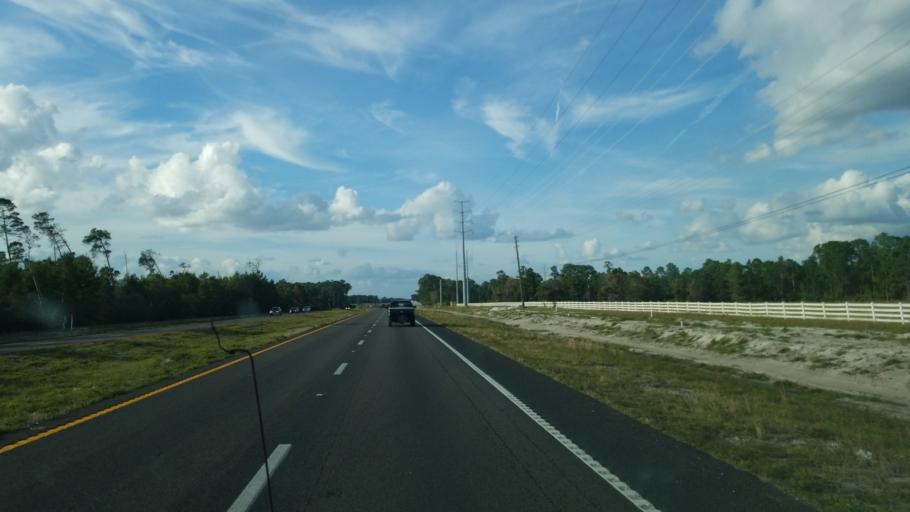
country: US
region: Florida
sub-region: Osceola County
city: Saint Cloud
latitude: 28.2149
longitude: -81.1758
